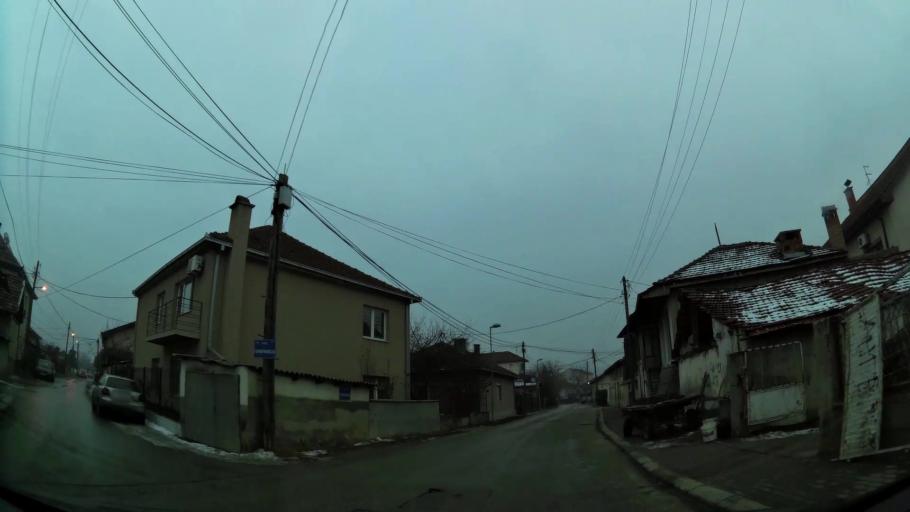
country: MK
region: Kisela Voda
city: Usje
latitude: 41.9703
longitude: 21.4820
